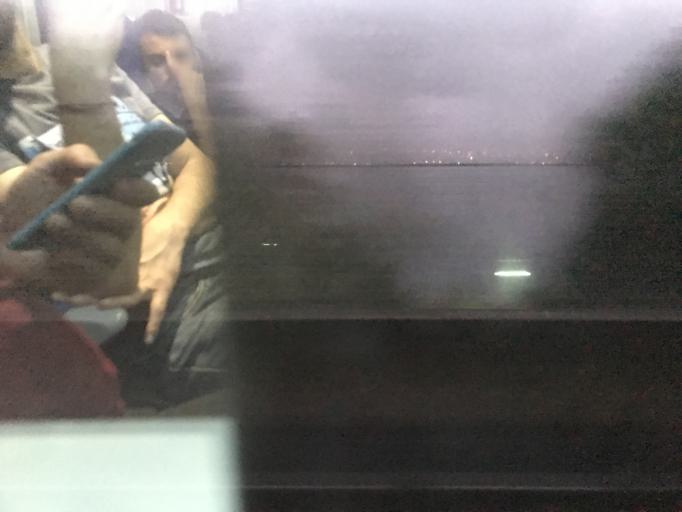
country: TR
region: Kocaeli
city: Derince
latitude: 40.7492
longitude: 29.8038
